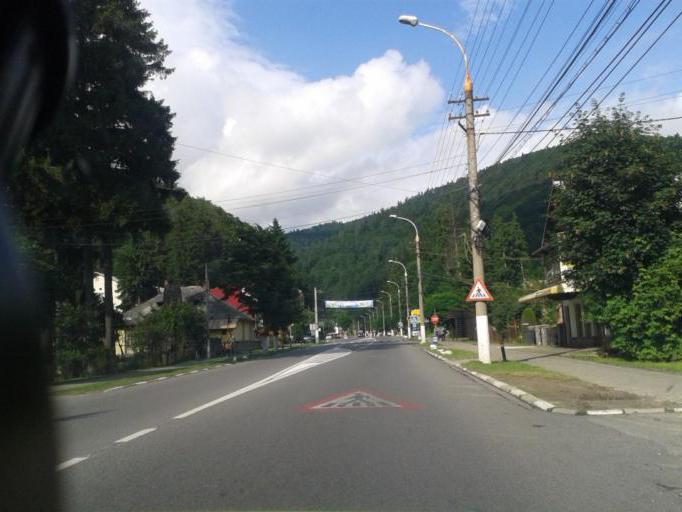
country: RO
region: Prahova
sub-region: Oras Busteni
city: Busteni
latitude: 45.4216
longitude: 25.5472
